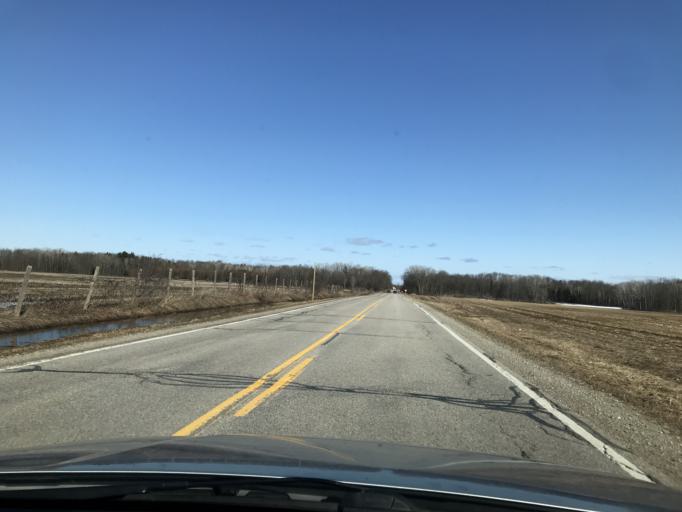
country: US
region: Wisconsin
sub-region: Marinette County
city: Peshtigo
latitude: 45.1792
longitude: -87.7738
